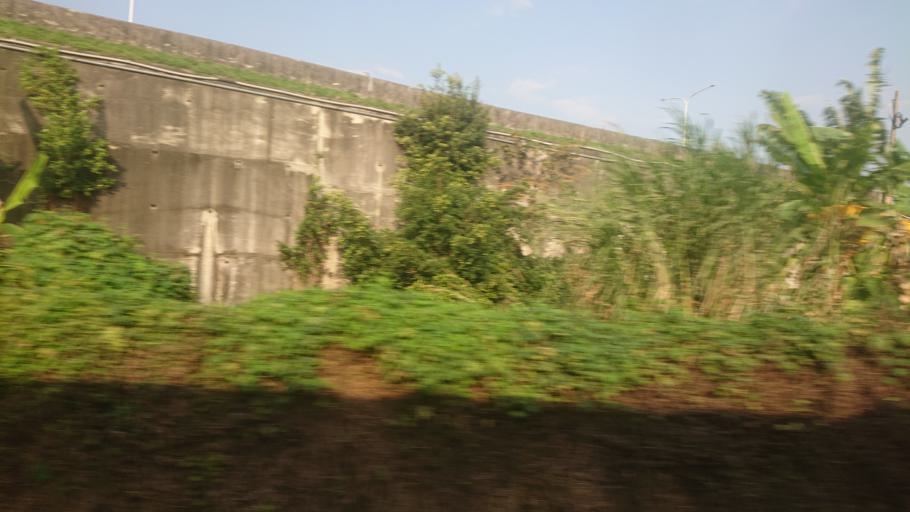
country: TW
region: Taiwan
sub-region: Chiayi
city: Jiayi Shi
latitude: 23.5880
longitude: 120.4433
